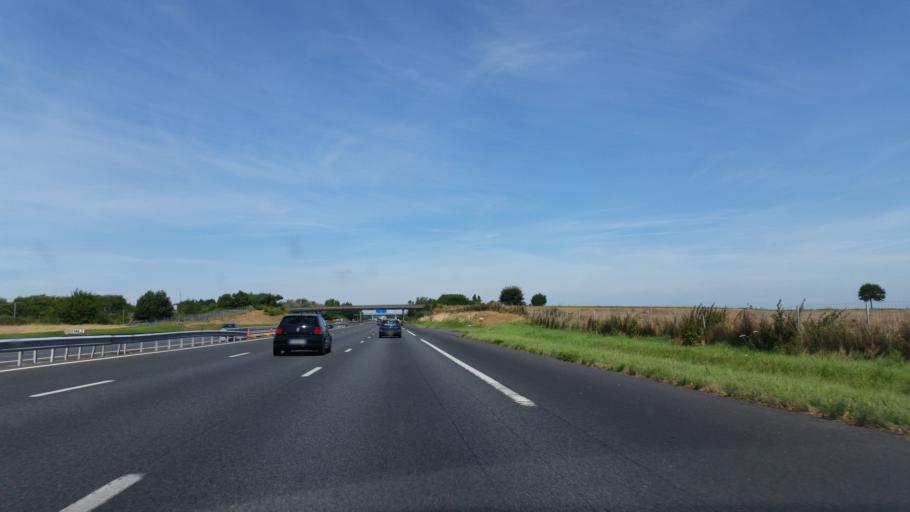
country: FR
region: Nord-Pas-de-Calais
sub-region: Departement du Pas-de-Calais
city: Bapaume
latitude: 50.0949
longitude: 2.8717
